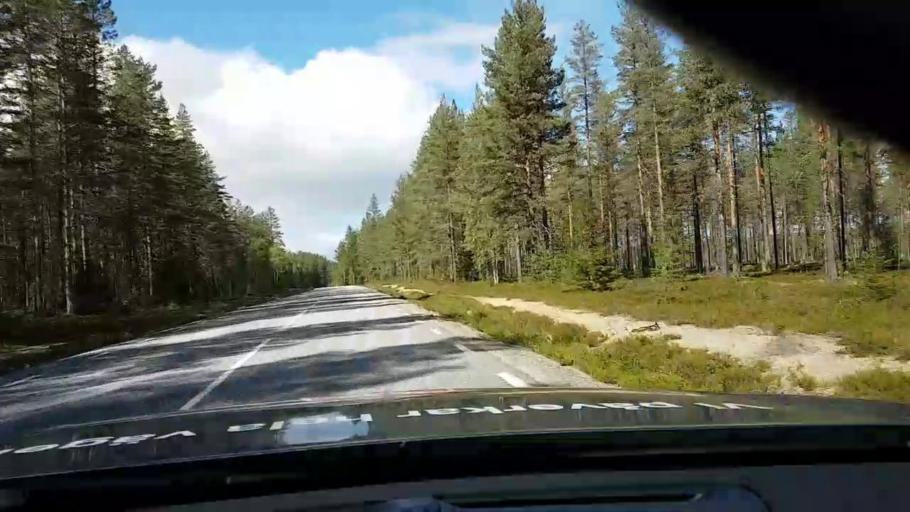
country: SE
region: Vaesternorrland
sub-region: OErnskoeldsviks Kommun
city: Bredbyn
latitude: 63.6655
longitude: 17.8343
